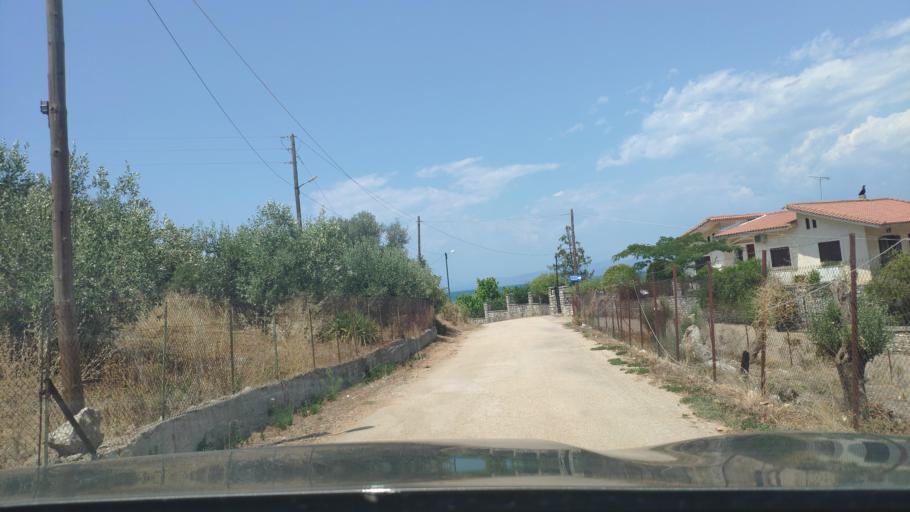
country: GR
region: West Greece
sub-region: Nomos Aitolias kai Akarnanias
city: Amfilochia
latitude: 38.8674
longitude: 21.0746
